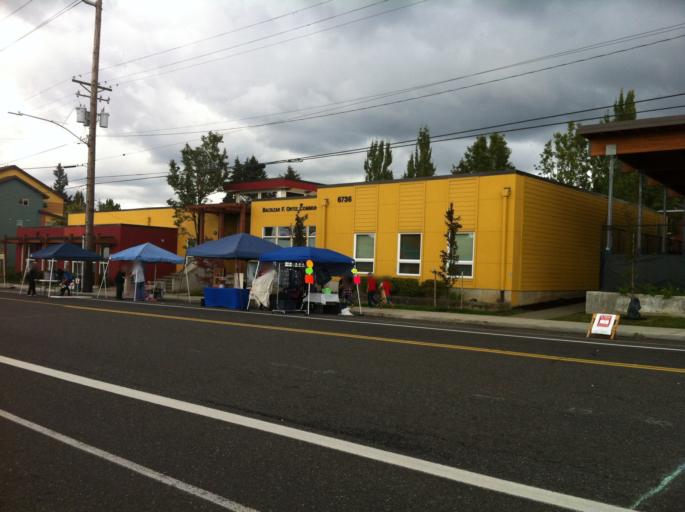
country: US
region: Oregon
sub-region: Multnomah County
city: Lents
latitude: 45.5627
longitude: -122.5936
